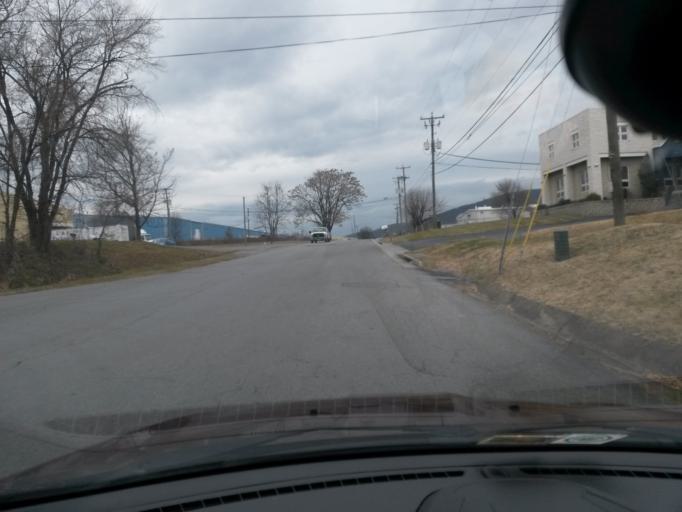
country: US
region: Virginia
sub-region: Roanoke County
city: Vinton
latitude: 37.3001
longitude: -79.8979
